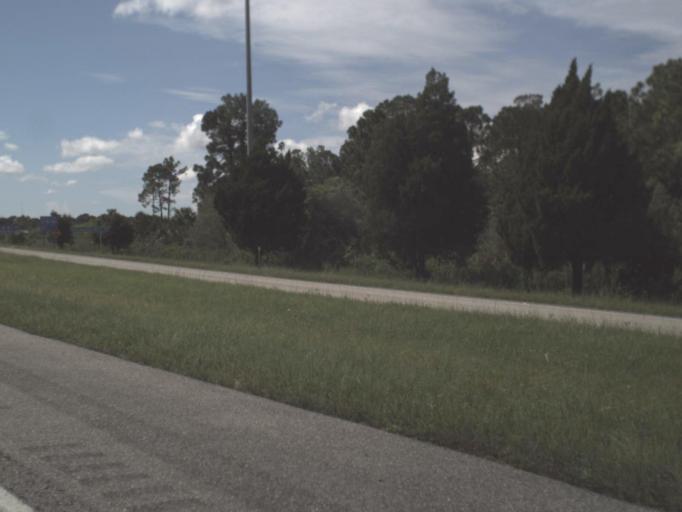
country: US
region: Florida
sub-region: Charlotte County
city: Harbour Heights
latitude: 27.0233
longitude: -82.0505
